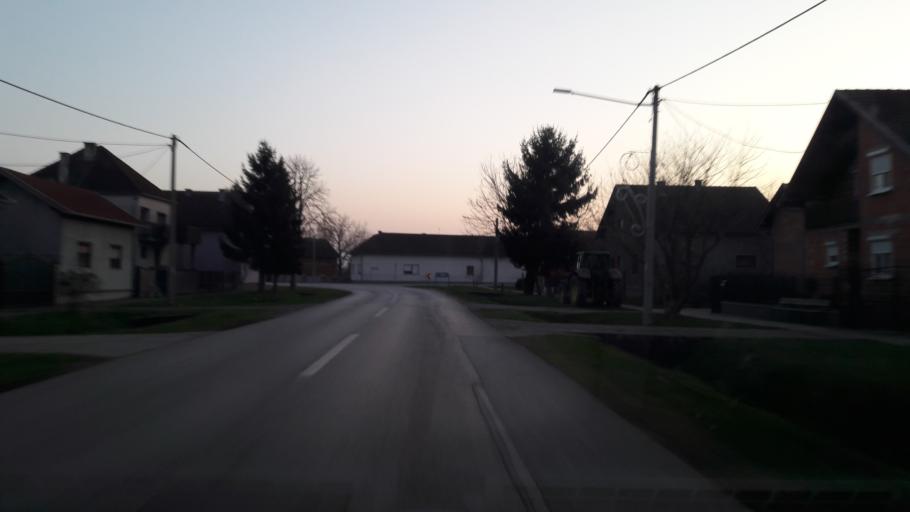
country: HR
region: Vukovarsko-Srijemska
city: Nijemci
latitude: 45.1800
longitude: 19.0116
